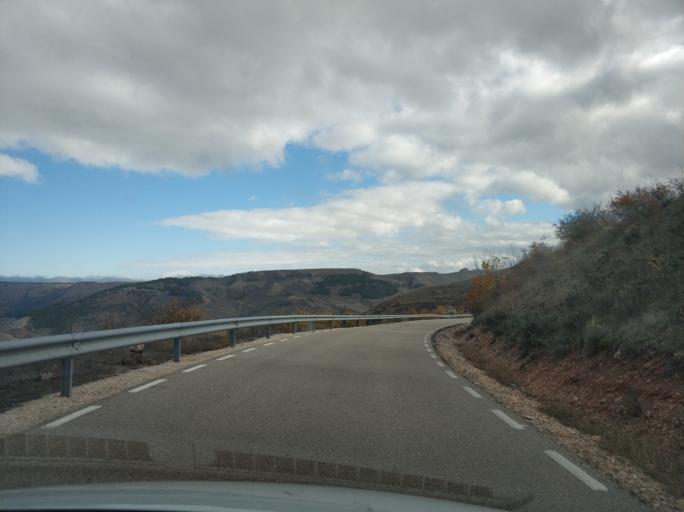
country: ES
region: Castille and Leon
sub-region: Provincia de Soria
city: Medinaceli
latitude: 41.1639
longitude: -2.4316
